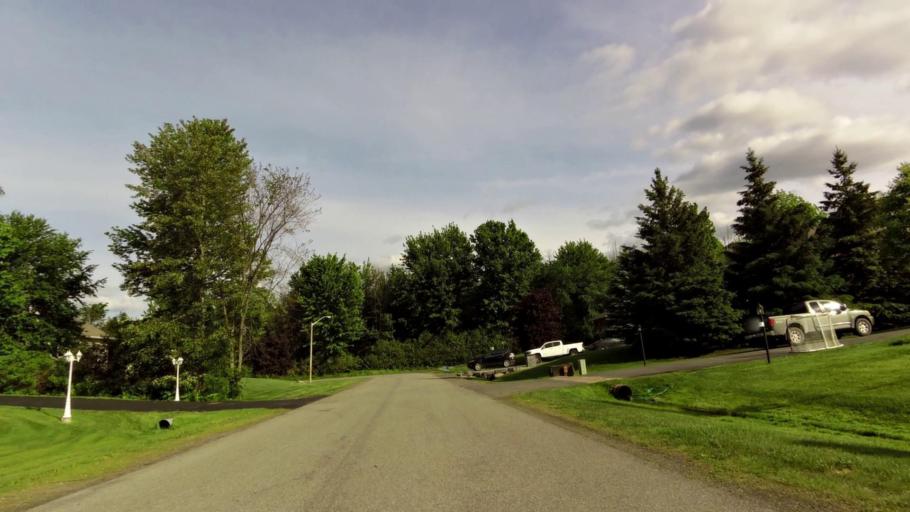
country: CA
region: Ontario
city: Ottawa
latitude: 45.2685
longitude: -75.5884
